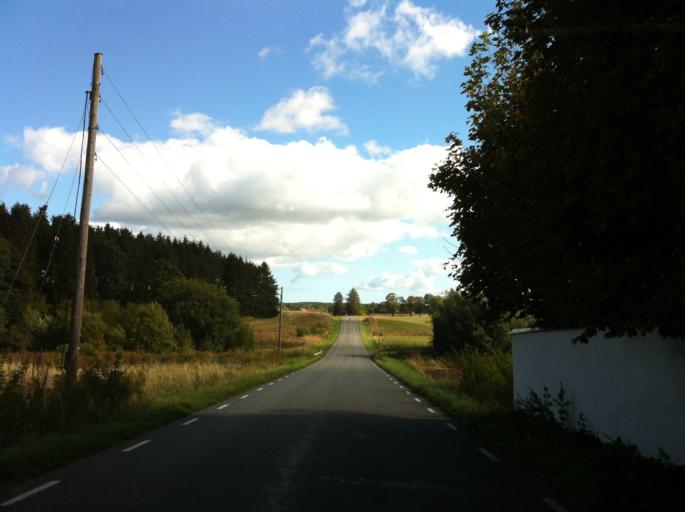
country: SE
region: Skane
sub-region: Kristianstads Kommun
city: Degeberga
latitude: 55.7047
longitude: 14.0074
